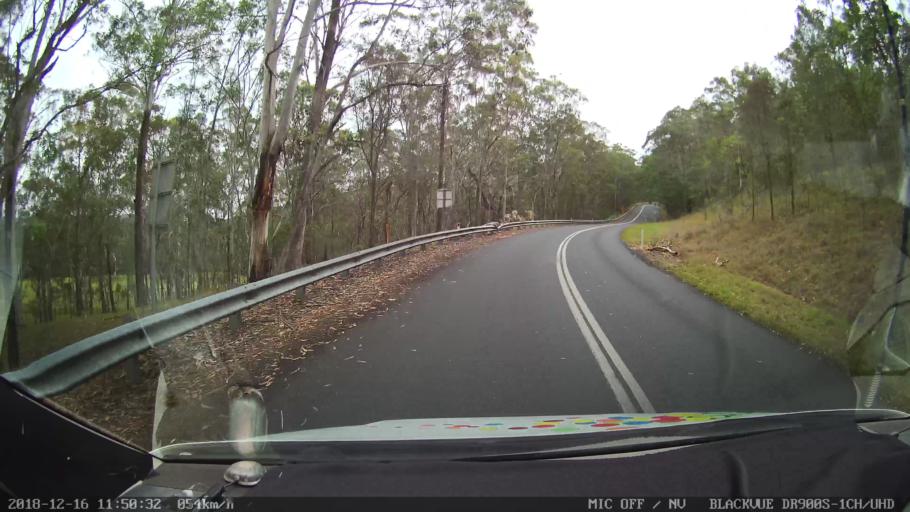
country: AU
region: New South Wales
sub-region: Tenterfield Municipality
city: Carrolls Creek
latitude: -28.9070
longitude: 152.2610
